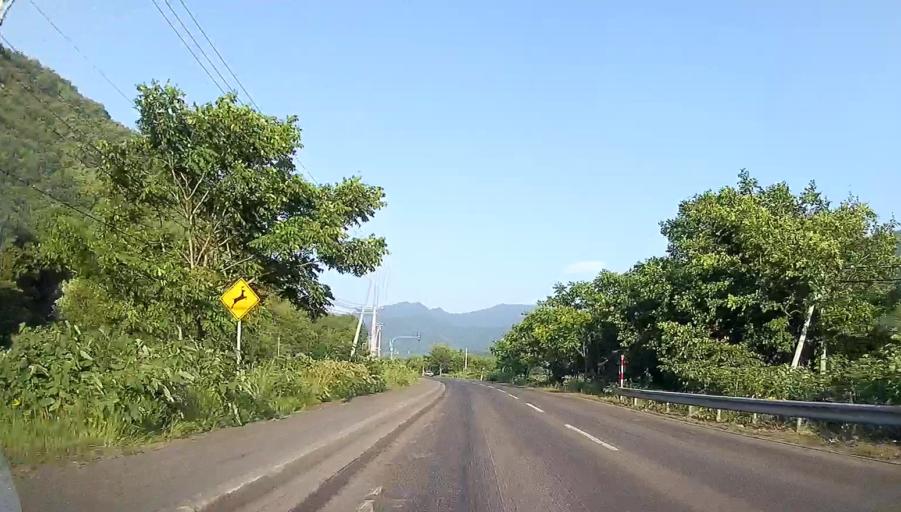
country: JP
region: Hokkaido
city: Shimo-furano
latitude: 42.8946
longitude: 142.5056
